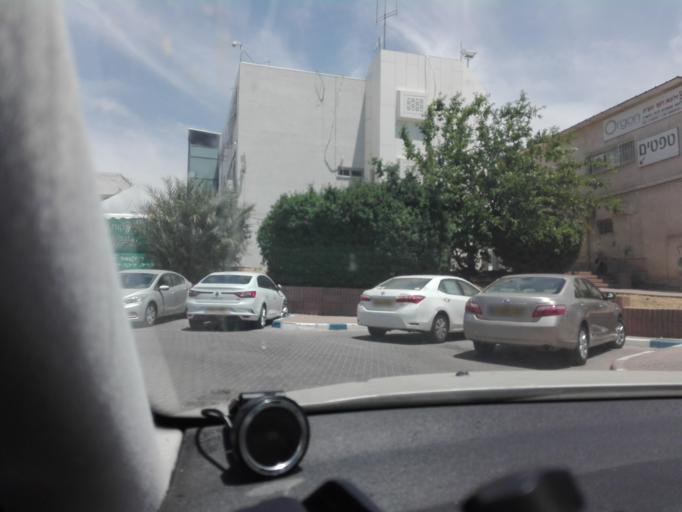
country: IL
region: Central District
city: Bene 'Ayish
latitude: 31.7297
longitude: 34.7467
